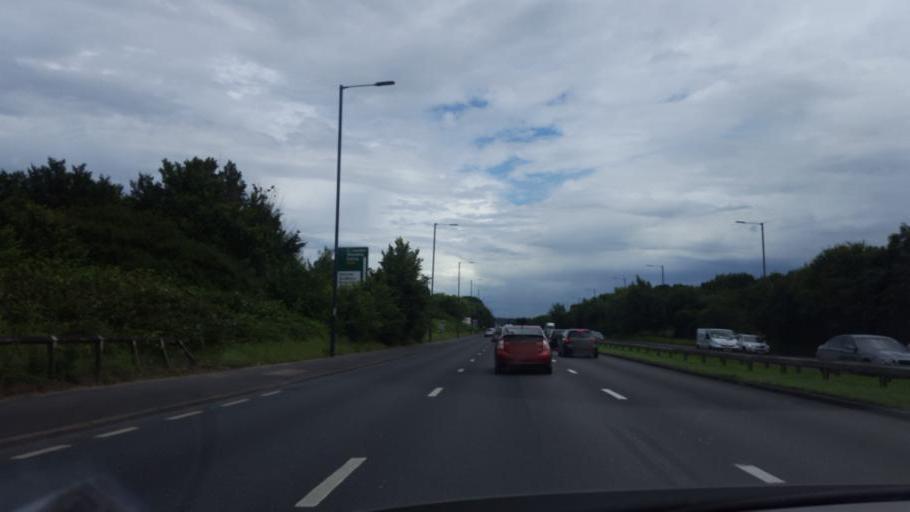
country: GB
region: England
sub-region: Greater London
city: Greenford
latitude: 51.5385
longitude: -0.3576
